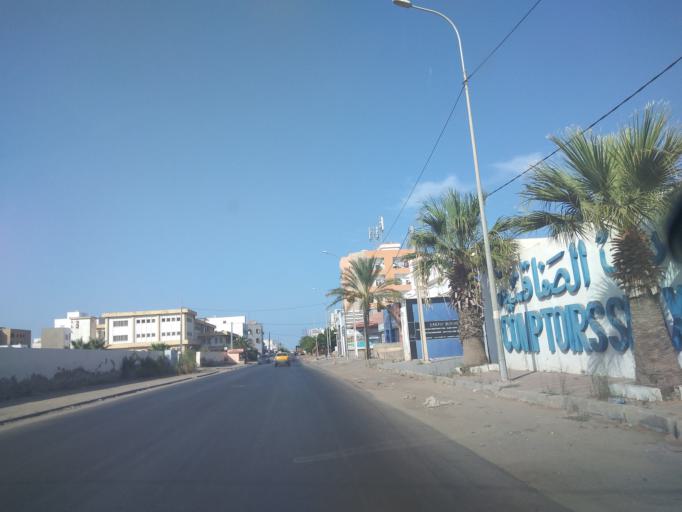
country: TN
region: Safaqis
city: Sfax
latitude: 34.7439
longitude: 10.7672
